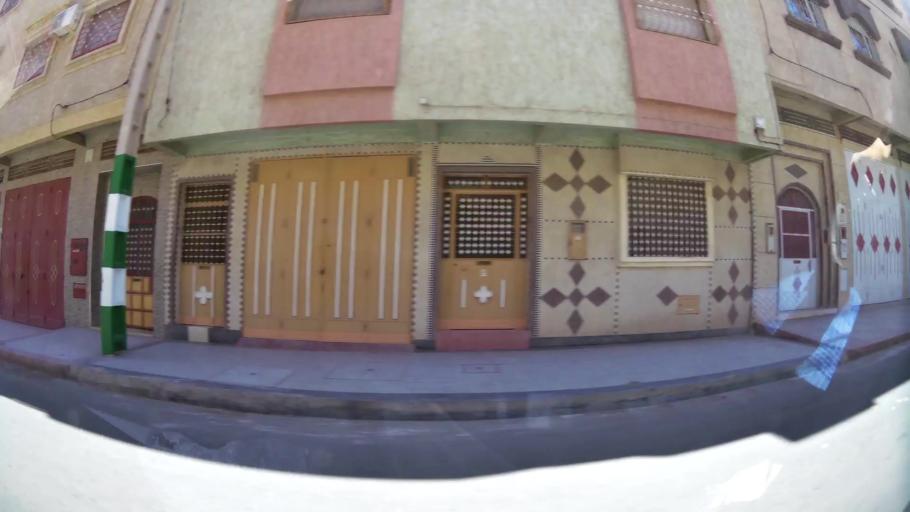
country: MA
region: Oriental
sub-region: Oujda-Angad
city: Oujda
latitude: 34.6546
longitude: -1.9350
